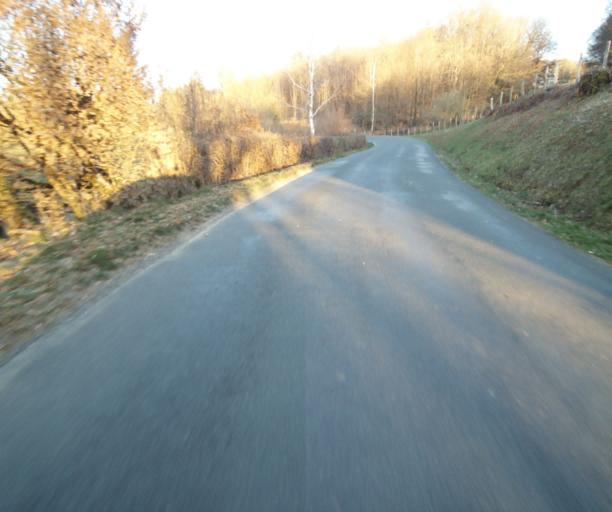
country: FR
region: Limousin
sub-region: Departement de la Correze
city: Saint-Clement
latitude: 45.3244
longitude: 1.6754
